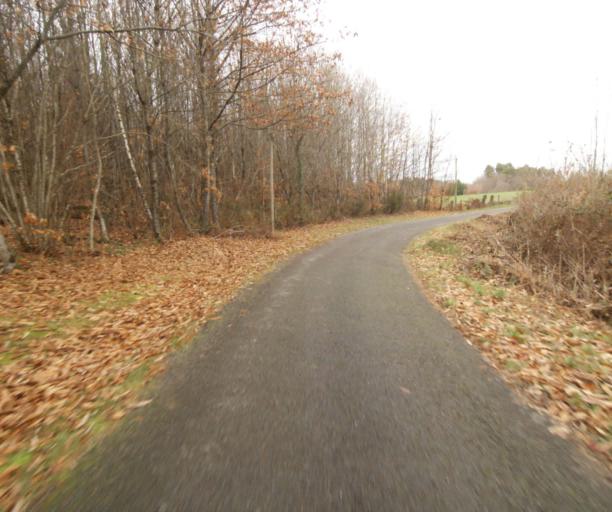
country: FR
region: Limousin
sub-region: Departement de la Correze
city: Chameyrat
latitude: 45.2331
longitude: 1.6837
